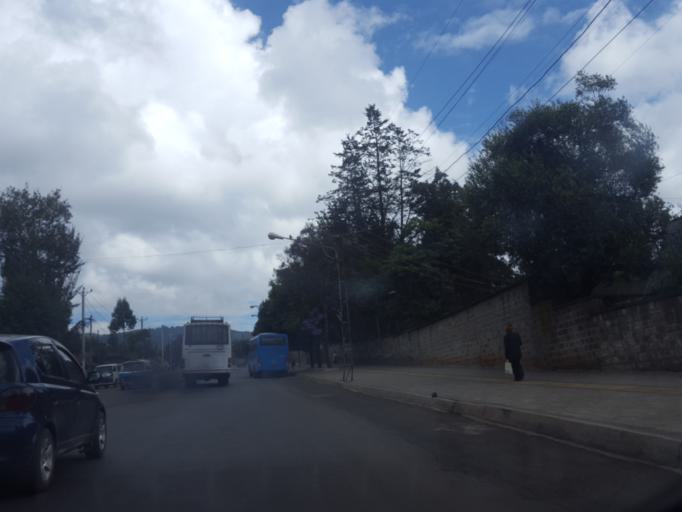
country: ET
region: Adis Abeba
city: Addis Ababa
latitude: 9.0543
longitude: 38.7626
